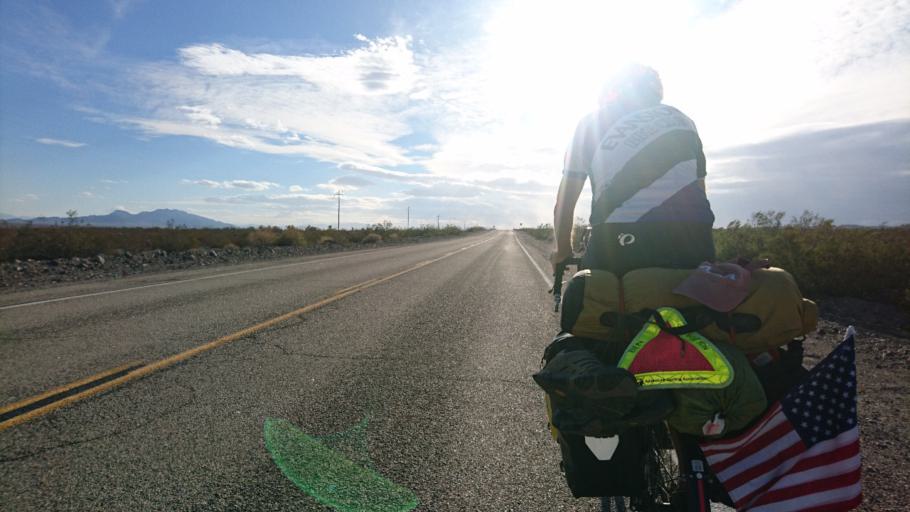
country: US
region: California
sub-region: San Bernardino County
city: Needles
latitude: 34.6788
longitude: -115.3285
